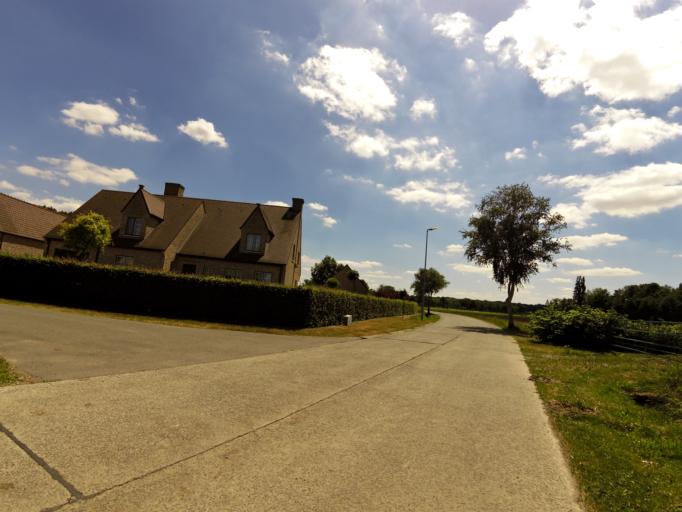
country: BE
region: Flanders
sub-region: Provincie West-Vlaanderen
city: Zedelgem
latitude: 51.1624
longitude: 3.1141
